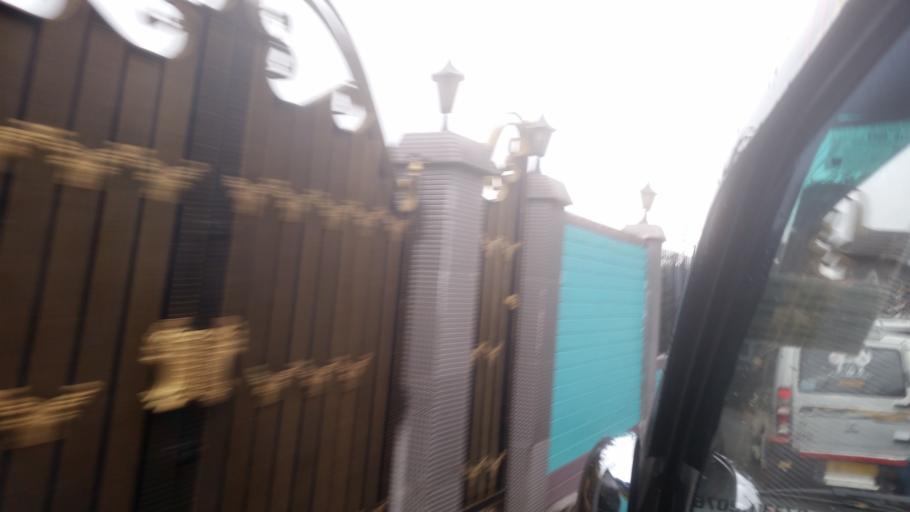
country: IN
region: West Bengal
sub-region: Darjiling
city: Darjiling
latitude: 27.0074
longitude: 88.2600
